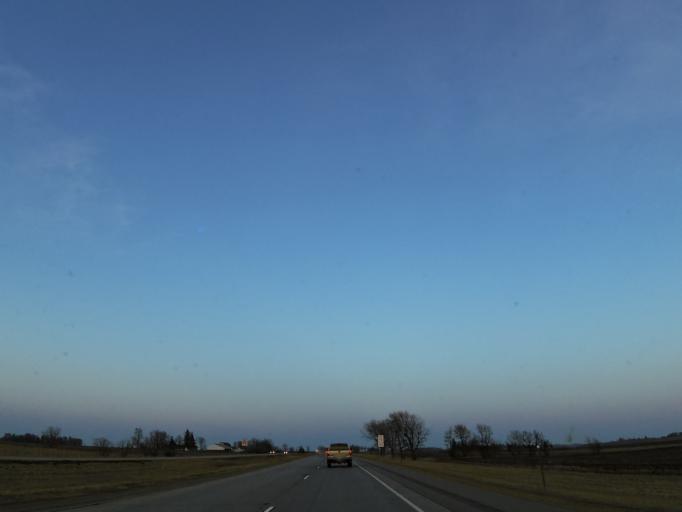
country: US
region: Minnesota
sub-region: Mower County
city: Austin
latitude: 43.6718
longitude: -92.8590
